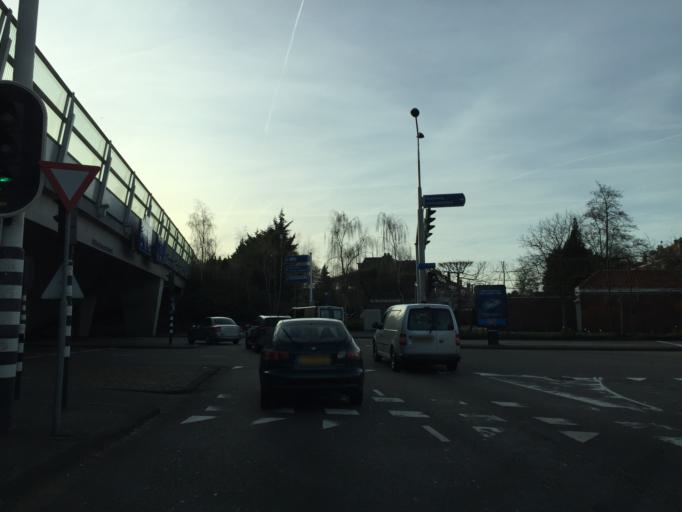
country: NL
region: South Holland
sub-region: Gemeente Leidschendam-Voorburg
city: Voorburg
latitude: 52.0684
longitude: 4.3561
